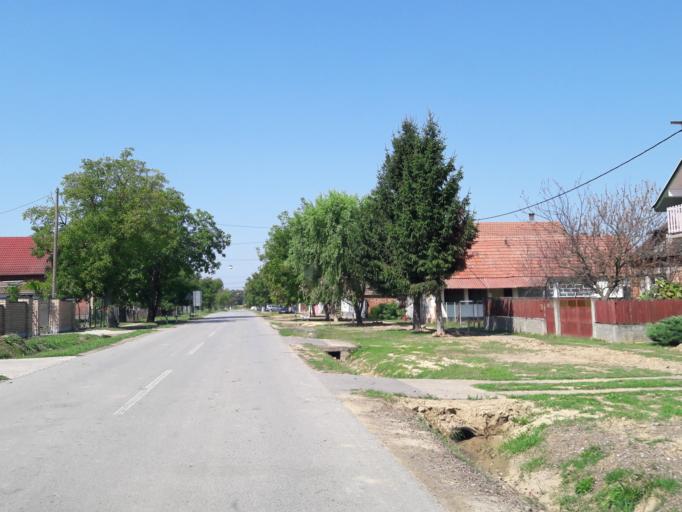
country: HR
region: Osjecko-Baranjska
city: Vuka
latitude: 45.4396
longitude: 18.4400
